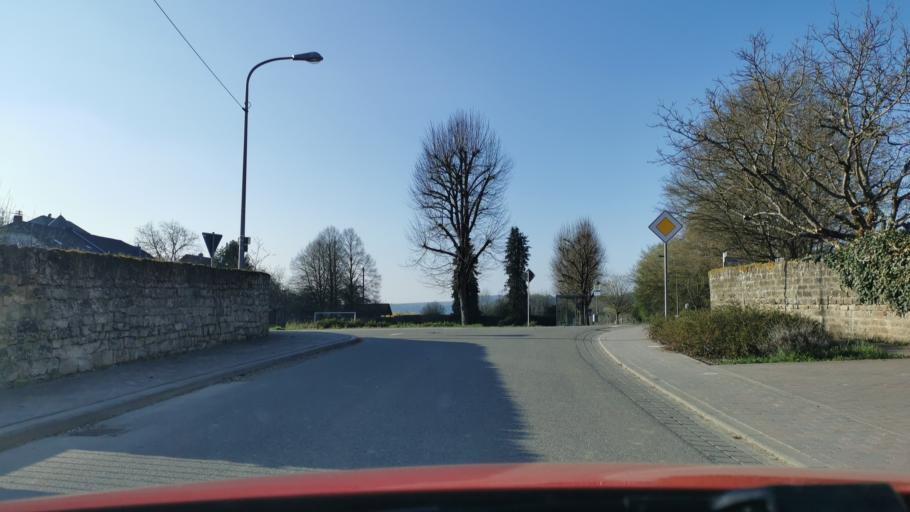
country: DE
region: Rheinland-Pfalz
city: Trierweiler
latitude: 49.7931
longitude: 6.5447
